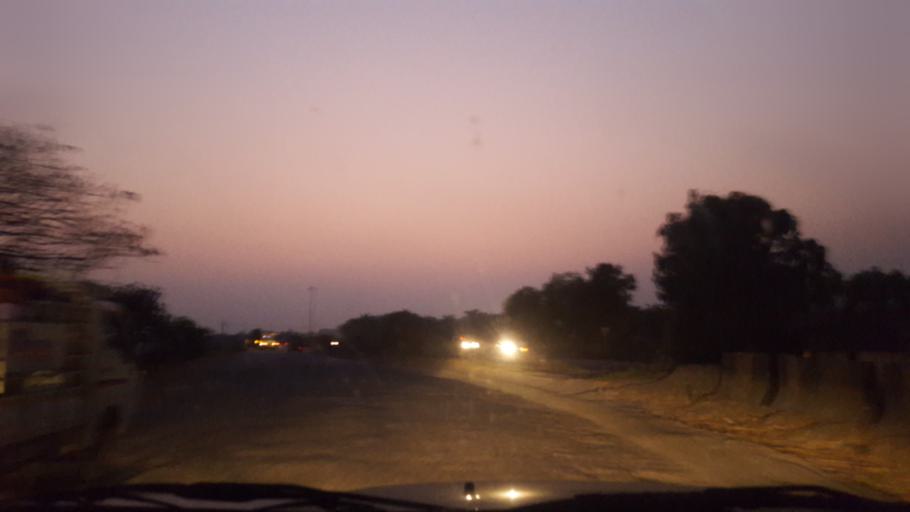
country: IN
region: Andhra Pradesh
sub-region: East Godavari
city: Rajahmundry
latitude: 17.1275
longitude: 81.9386
